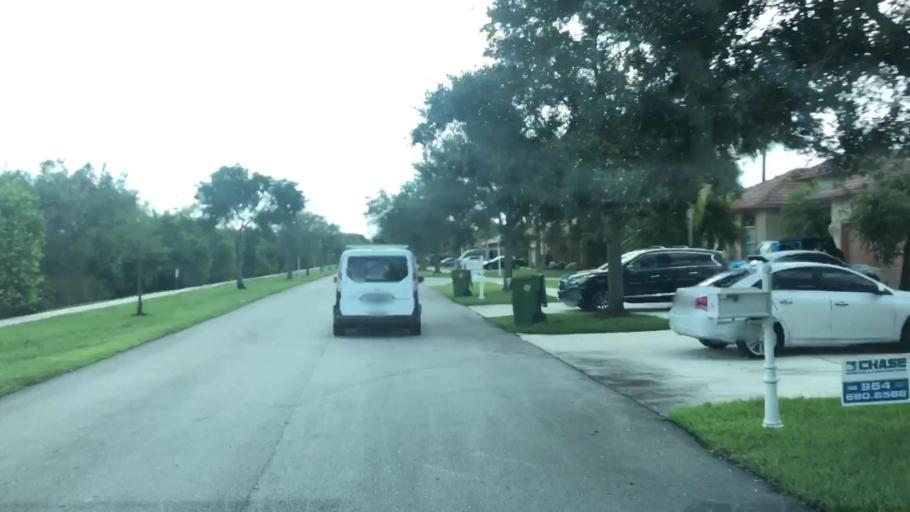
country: US
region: Florida
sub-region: Broward County
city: Southwest Ranches
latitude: 26.0345
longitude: -80.3671
